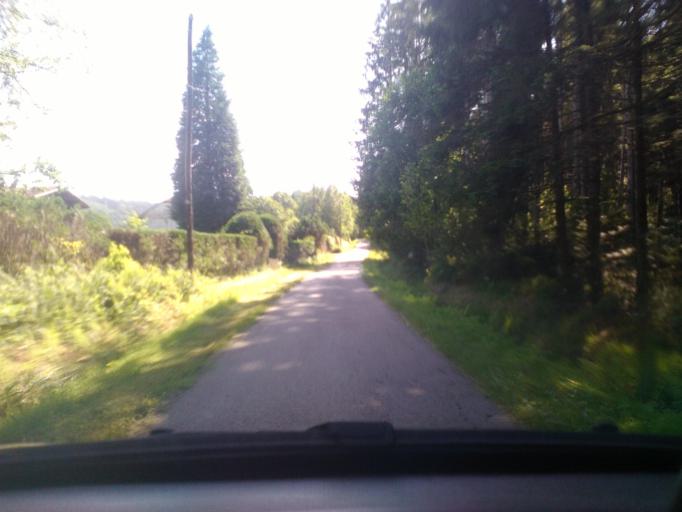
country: FR
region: Lorraine
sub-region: Departement des Vosges
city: Etival-Clairefontaine
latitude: 48.3111
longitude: 6.8016
